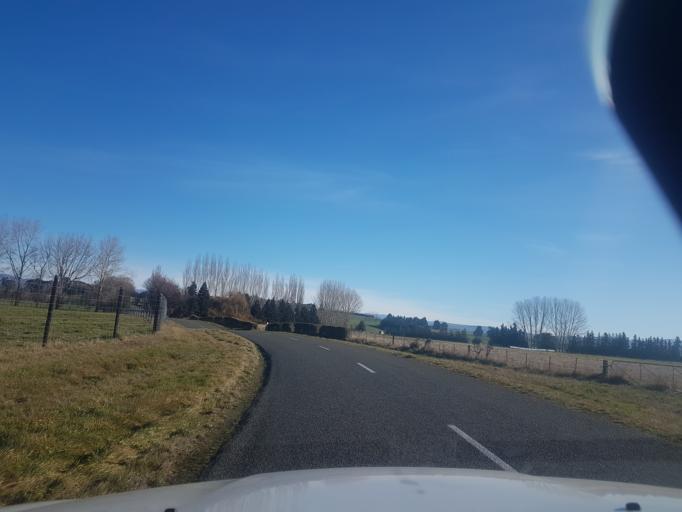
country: NZ
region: Canterbury
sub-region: Timaru District
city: Pleasant Point
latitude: -44.2448
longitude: 171.0911
